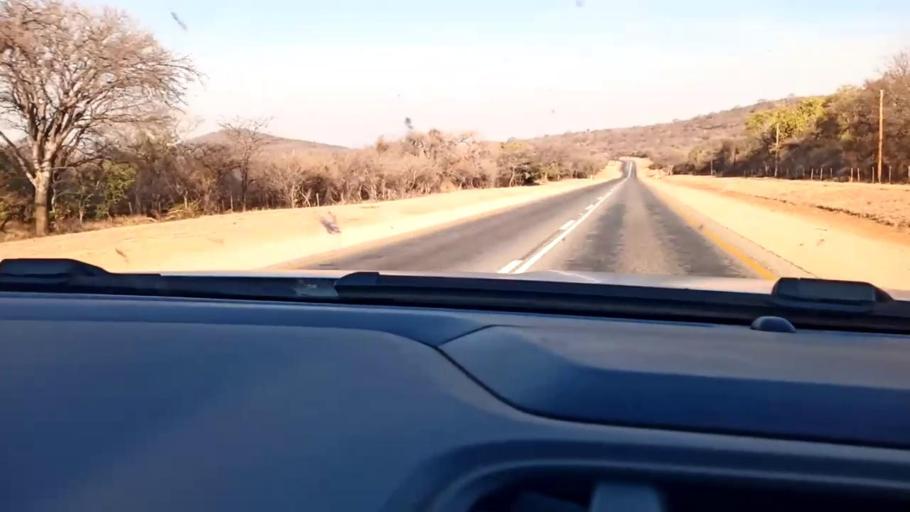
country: ZA
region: Limpopo
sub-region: Mopani District Municipality
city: Duiwelskloof
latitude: -23.6320
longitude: 30.1359
